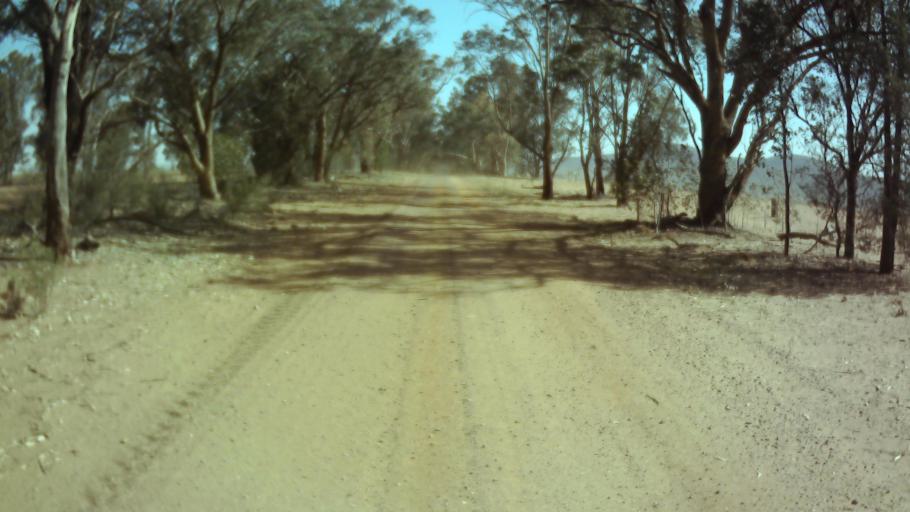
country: AU
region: New South Wales
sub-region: Weddin
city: Grenfell
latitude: -33.8474
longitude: 148.0170
